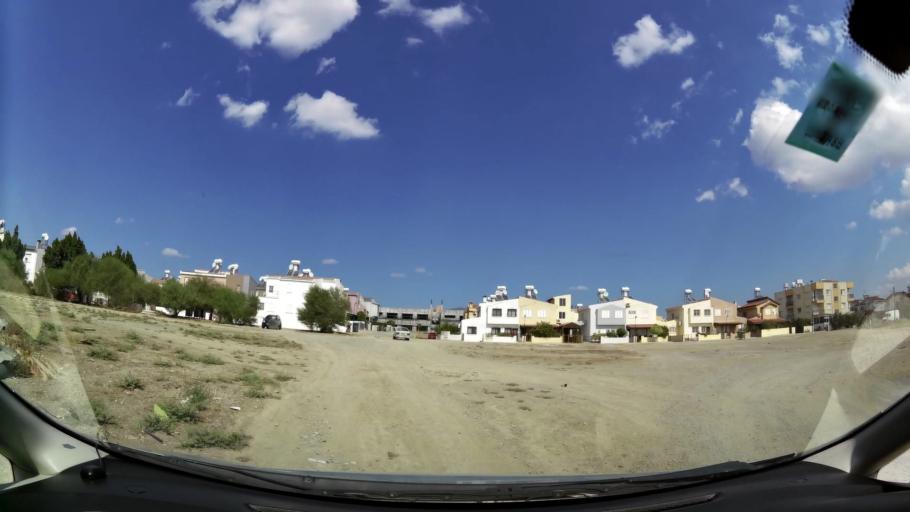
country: CY
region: Lefkosia
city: Nicosia
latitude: 35.2233
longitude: 33.2945
